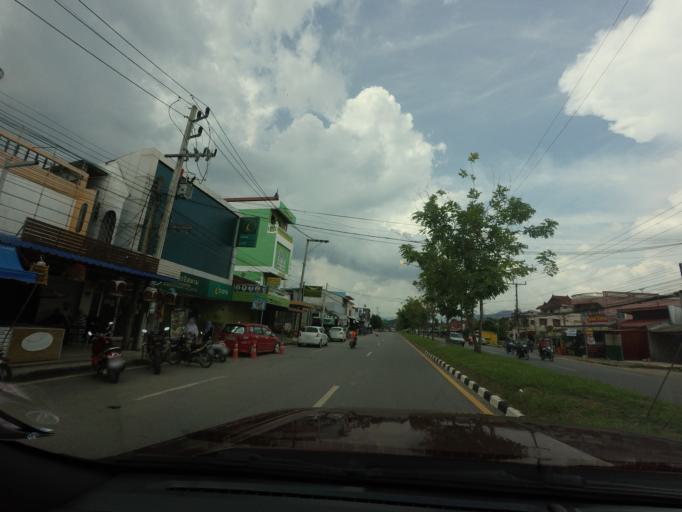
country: TH
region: Yala
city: Ban Nang Sata
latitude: 6.2636
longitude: 101.2594
